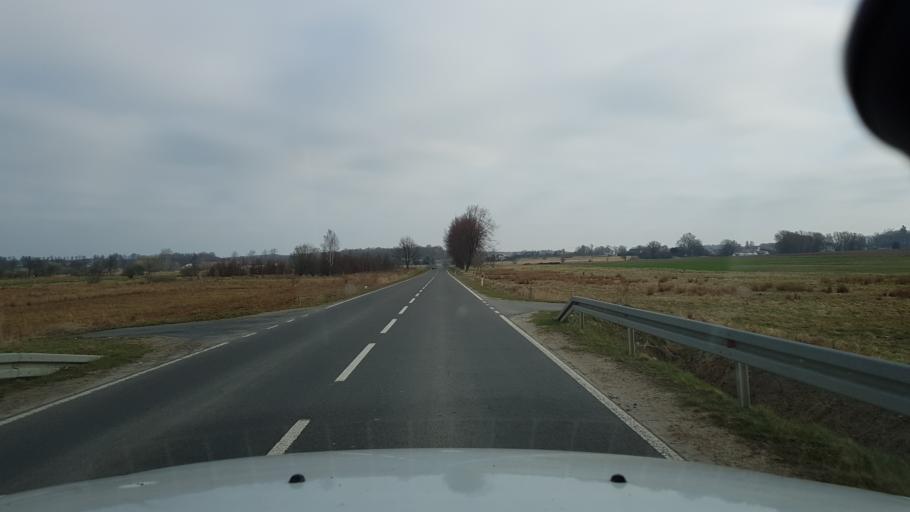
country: PL
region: West Pomeranian Voivodeship
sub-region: Powiat koszalinski
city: Sianow
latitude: 54.2391
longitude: 16.2763
